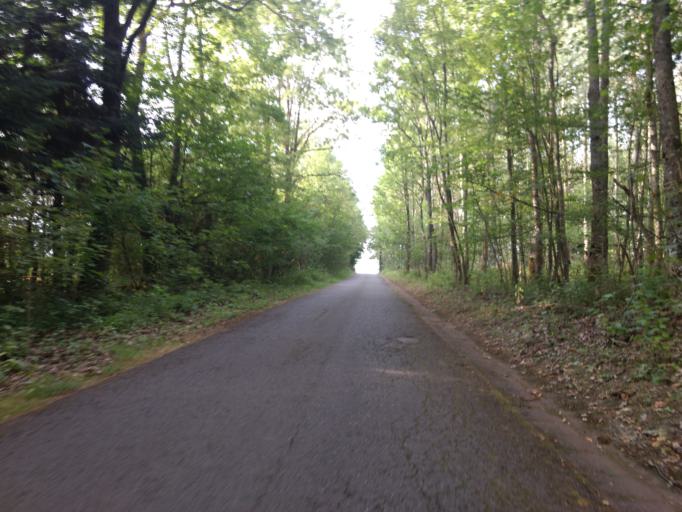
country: DE
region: Saarland
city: Rehlingen-Siersburg
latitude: 49.3426
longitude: 6.6847
